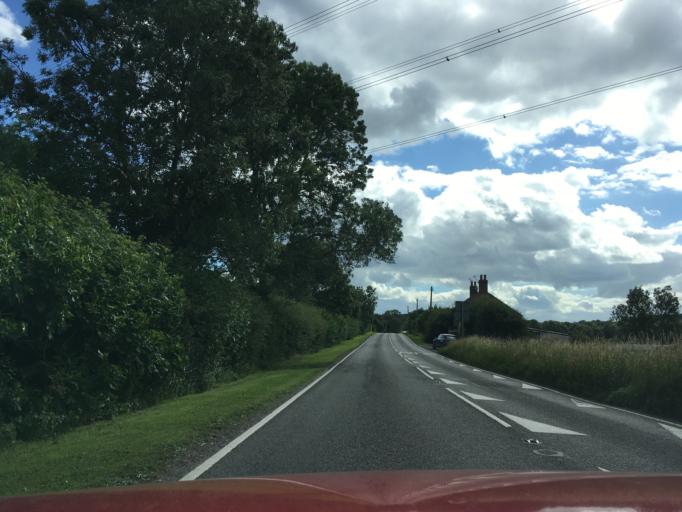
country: GB
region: England
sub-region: Leicestershire
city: Coalville
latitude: 52.7648
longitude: -1.3959
